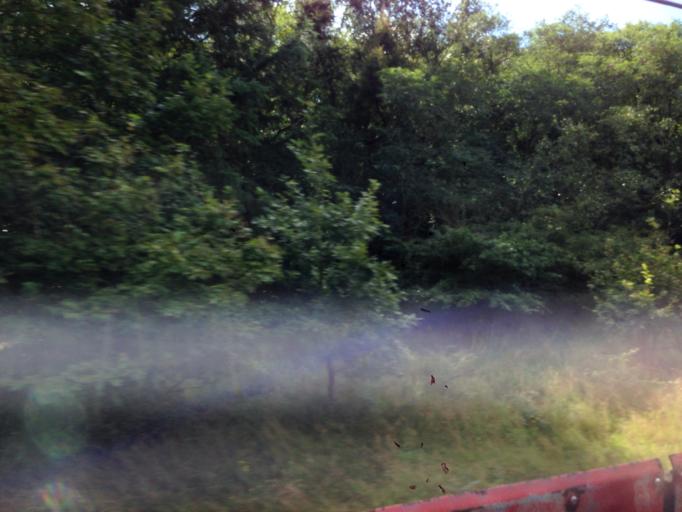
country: DE
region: Schleswig-Holstein
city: Sylt-Ost
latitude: 54.8707
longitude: 8.4599
